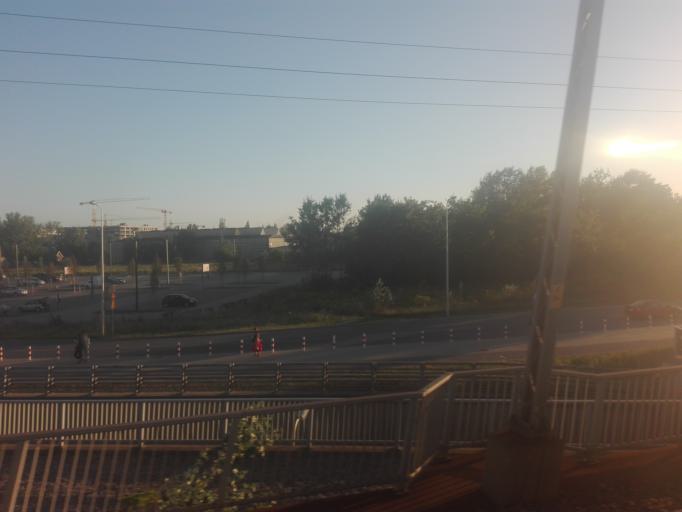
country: PL
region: Masovian Voivodeship
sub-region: Warszawa
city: Ursus
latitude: 52.2045
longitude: 20.8927
